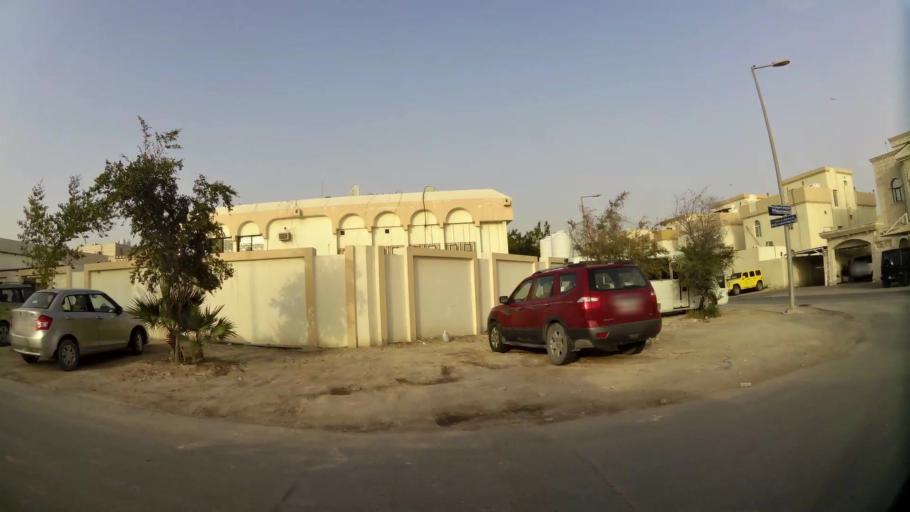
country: QA
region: Baladiyat ar Rayyan
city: Ar Rayyan
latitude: 25.2413
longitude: 51.4526
